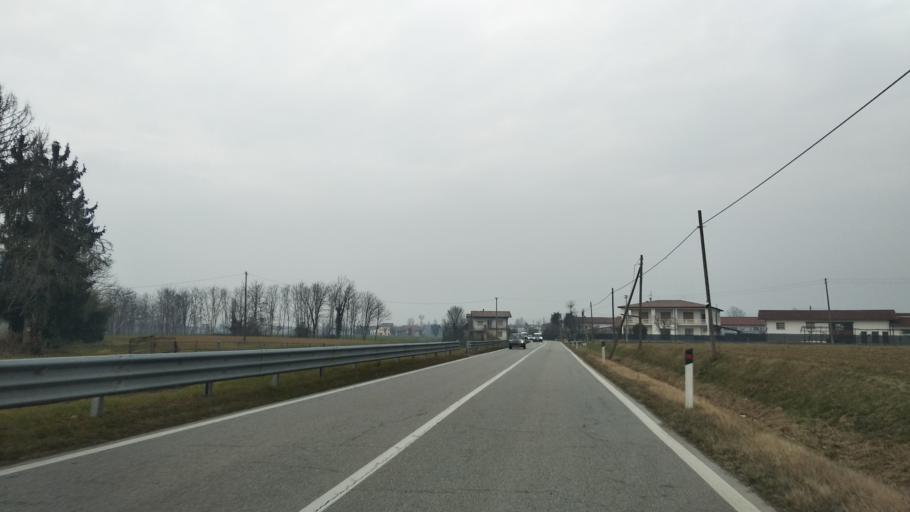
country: IT
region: Veneto
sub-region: Provincia di Padova
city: Villa del Conte
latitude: 45.5660
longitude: 11.8658
